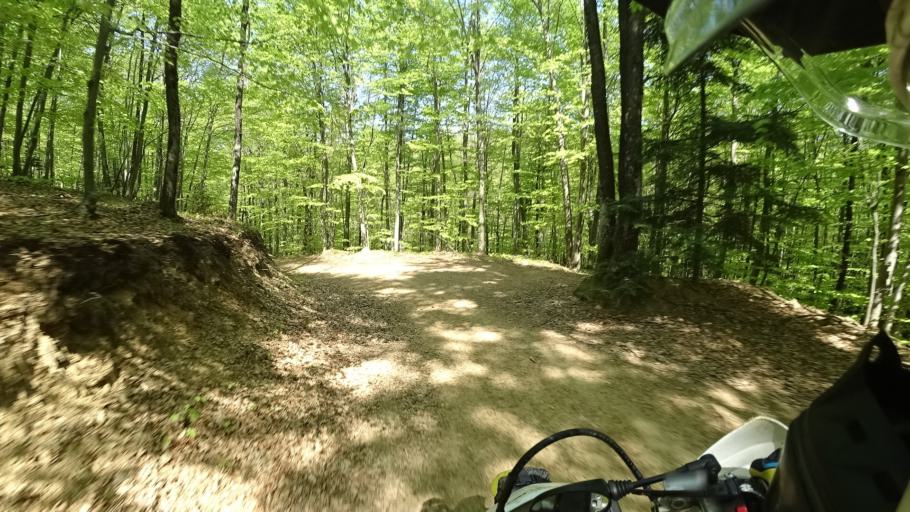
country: HR
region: Zagrebacka
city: Jablanovec
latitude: 45.9076
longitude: 15.9133
